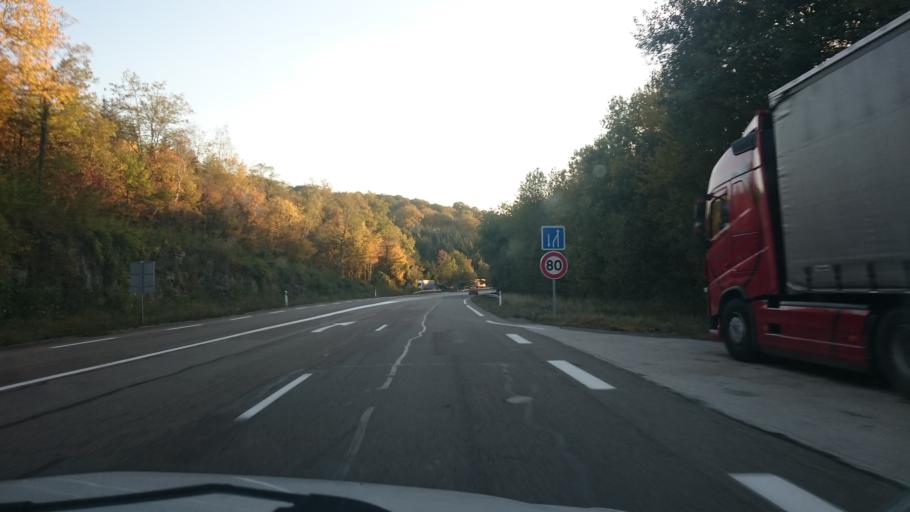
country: FR
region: Franche-Comte
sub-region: Departement du Jura
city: Mouchard
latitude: 46.9689
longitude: 5.8003
